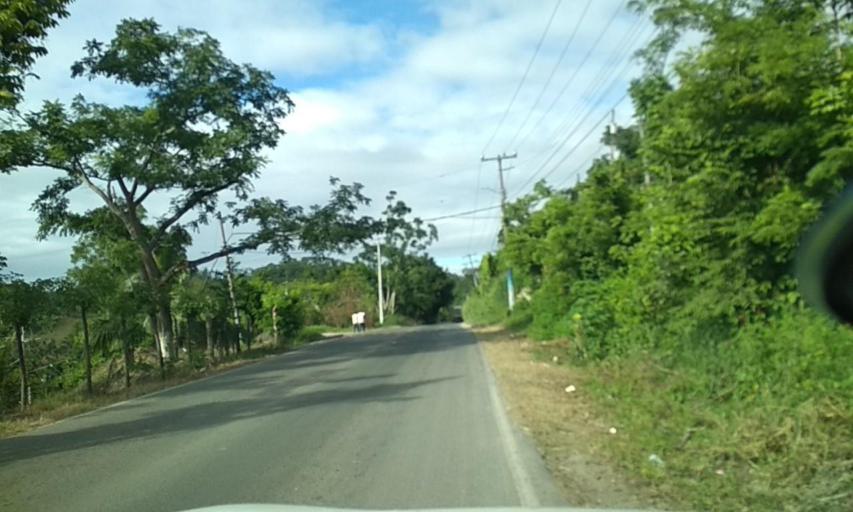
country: MX
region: Veracruz
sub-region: Papantla
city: Residencial Tajin
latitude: 20.6445
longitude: -97.3603
